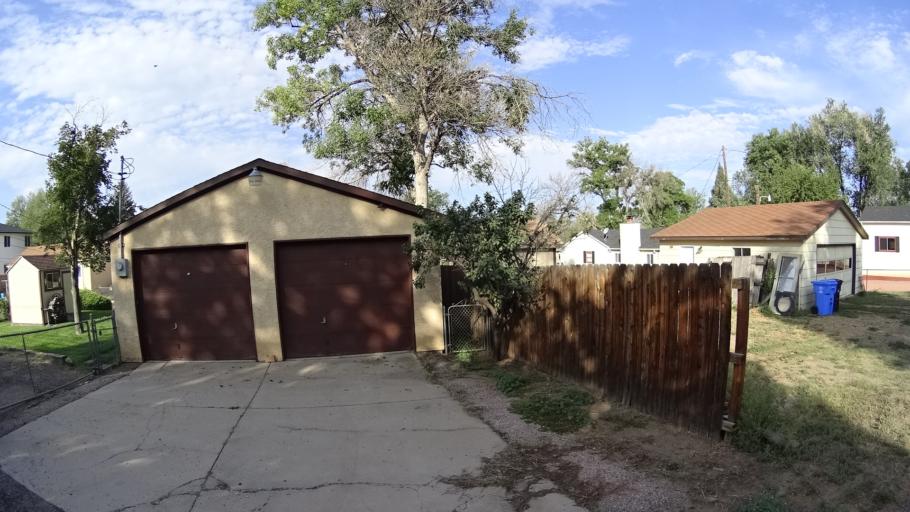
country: US
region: Colorado
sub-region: El Paso County
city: Colorado Springs
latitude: 38.8557
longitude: -104.7719
